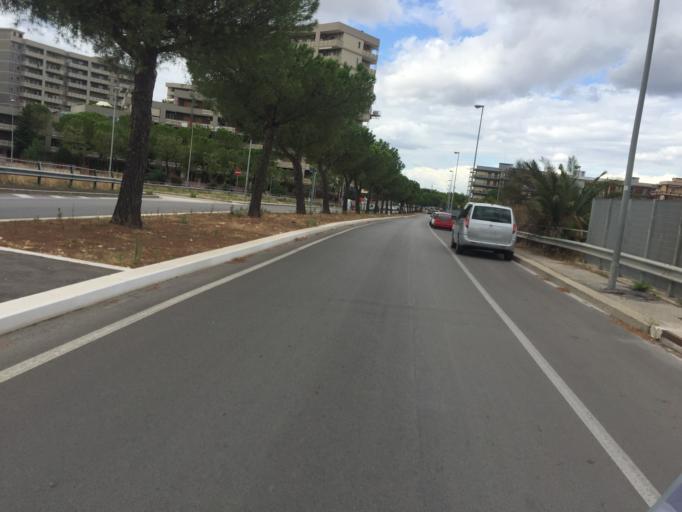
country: IT
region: Apulia
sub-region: Provincia di Bari
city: Bari
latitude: 41.0933
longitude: 16.8580
